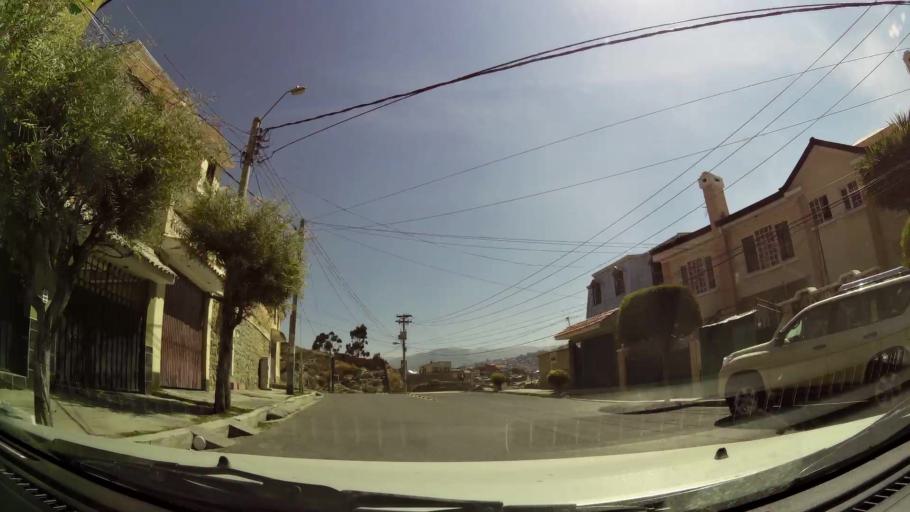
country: BO
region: La Paz
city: La Paz
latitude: -16.5361
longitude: -68.1022
